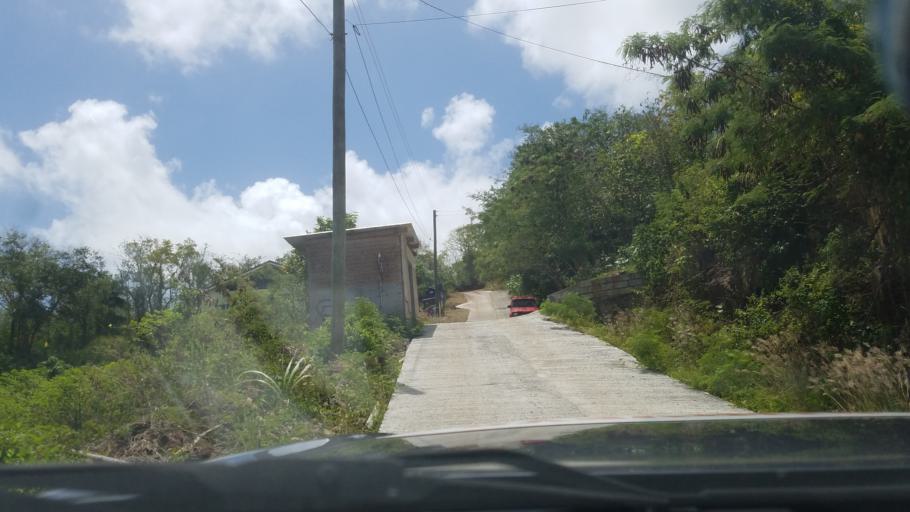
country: LC
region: Gros-Islet
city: Gros Islet
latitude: 14.0645
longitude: -60.9348
